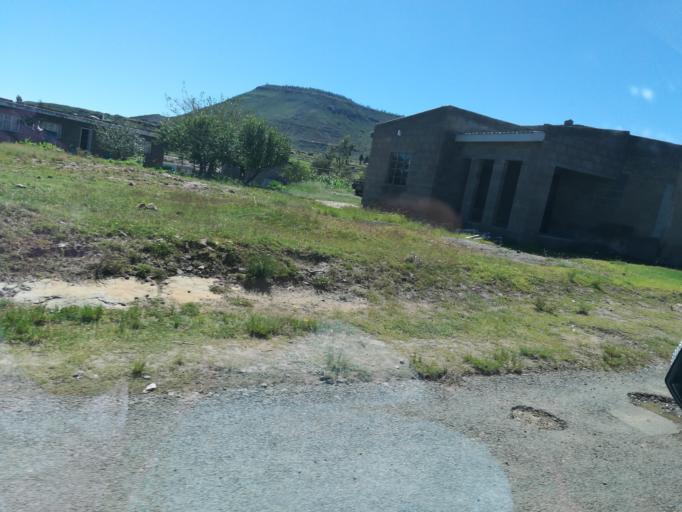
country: LS
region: Mohale's Hoek District
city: Mohale's Hoek
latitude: -30.1081
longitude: 27.4728
